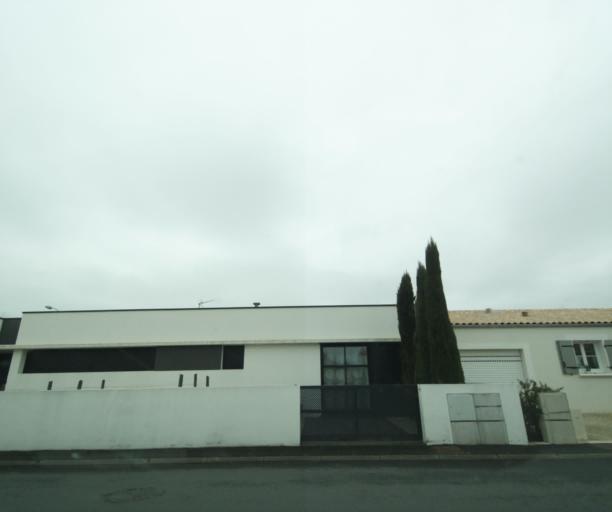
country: FR
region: Poitou-Charentes
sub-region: Departement de la Charente-Maritime
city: Lagord
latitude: 46.1862
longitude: -1.1408
